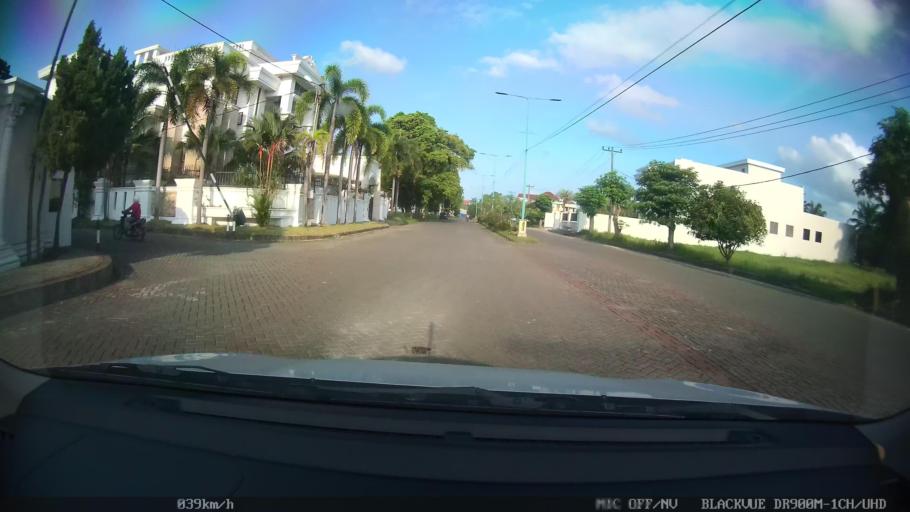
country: ID
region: North Sumatra
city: Medan
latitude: 3.6252
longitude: 98.6484
